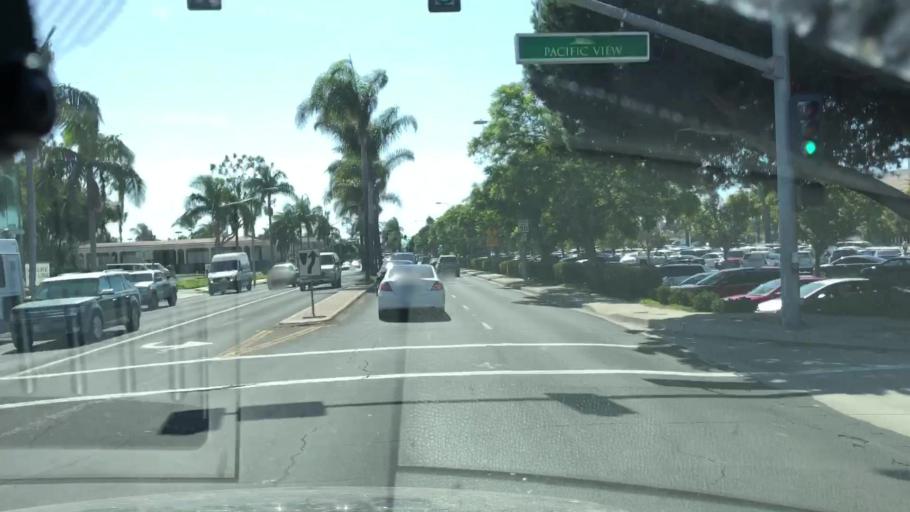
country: US
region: California
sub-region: Ventura County
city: Ventura
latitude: 34.2689
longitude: -119.2469
